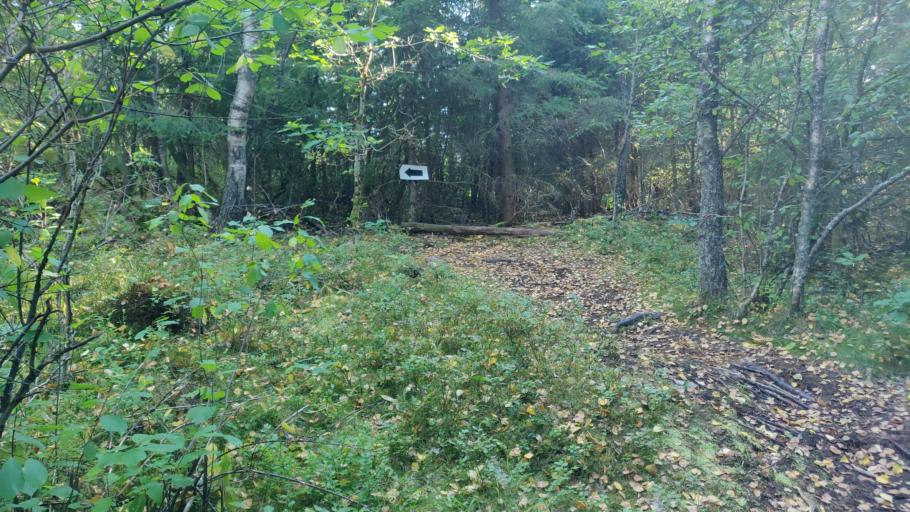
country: SE
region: Vaestra Goetaland
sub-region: Uddevalla Kommun
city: Uddevalla
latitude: 58.3691
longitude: 11.9540
